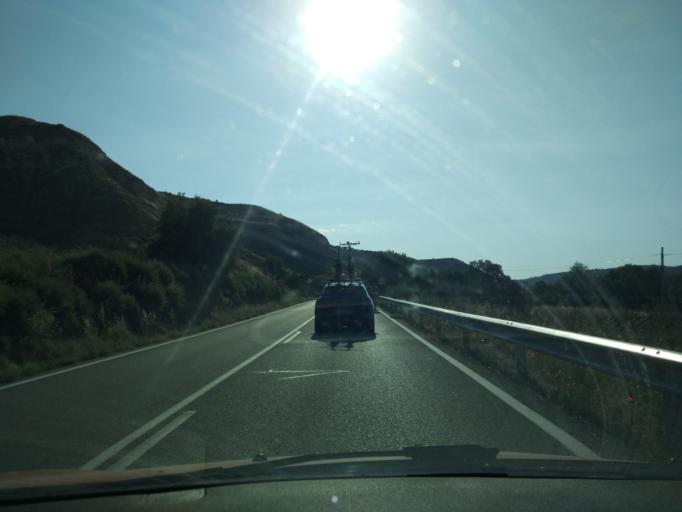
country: ES
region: Madrid
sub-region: Provincia de Madrid
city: Valverde de Alcala
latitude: 40.4173
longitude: -3.3154
